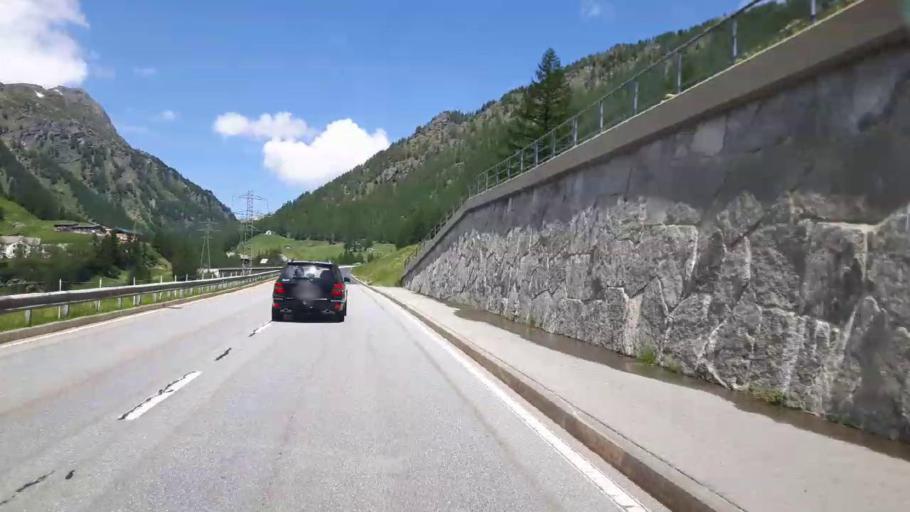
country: IT
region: Piedmont
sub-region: Provincia Verbano-Cusio-Ossola
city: Antronapiana
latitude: 46.1946
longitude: 8.0631
